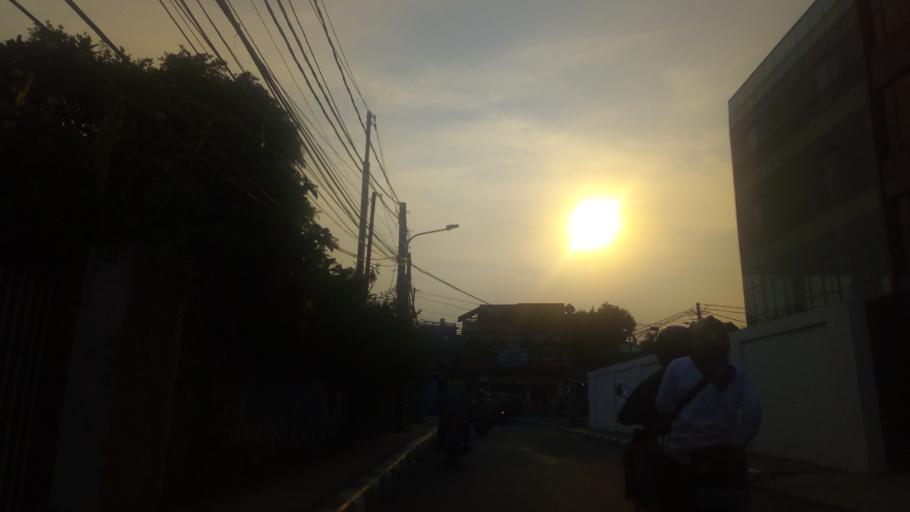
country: ID
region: Jakarta Raya
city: Jakarta
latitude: -6.2039
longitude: 106.8499
